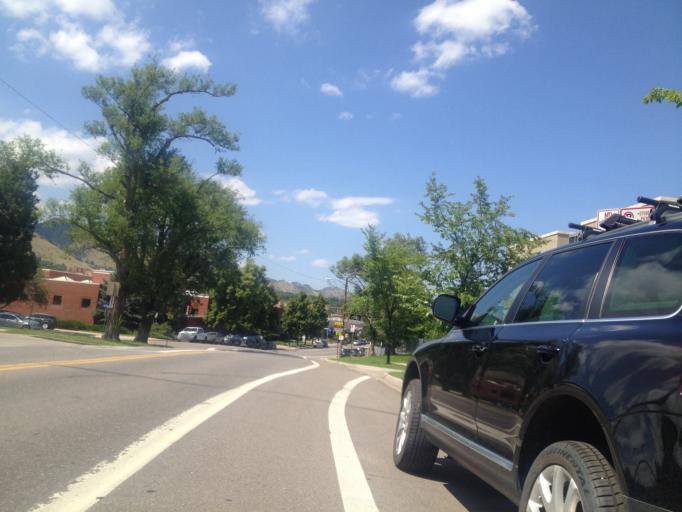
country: US
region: Colorado
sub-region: Boulder County
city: Boulder
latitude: 40.0229
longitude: -105.2803
